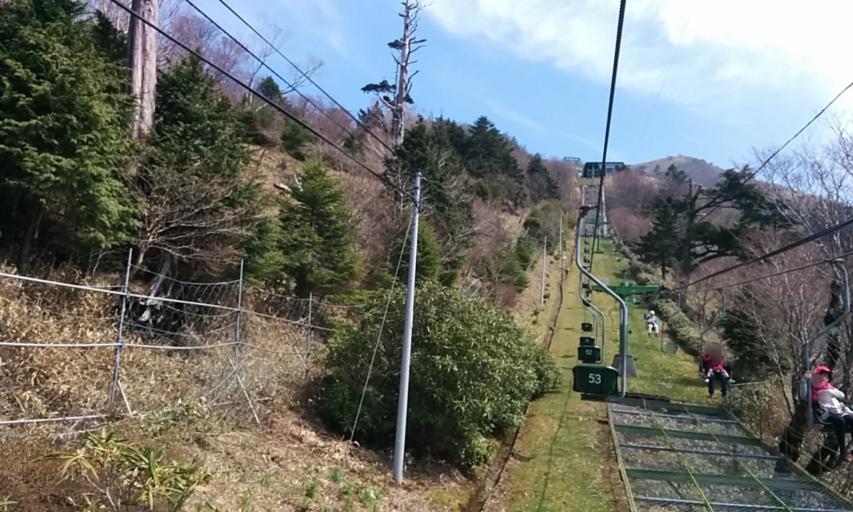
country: JP
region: Tokushima
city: Wakimachi
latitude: 33.8624
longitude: 134.0913
